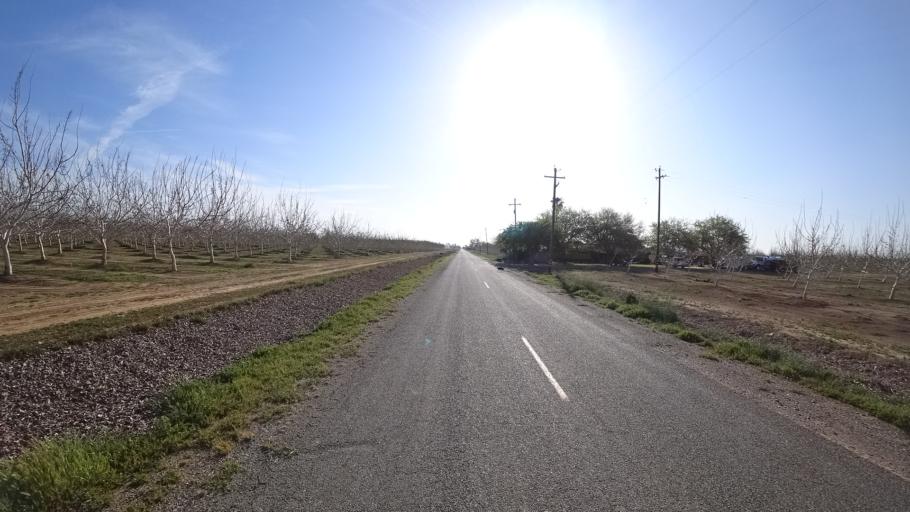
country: US
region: California
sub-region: Glenn County
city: Willows
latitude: 39.5096
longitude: -122.2453
